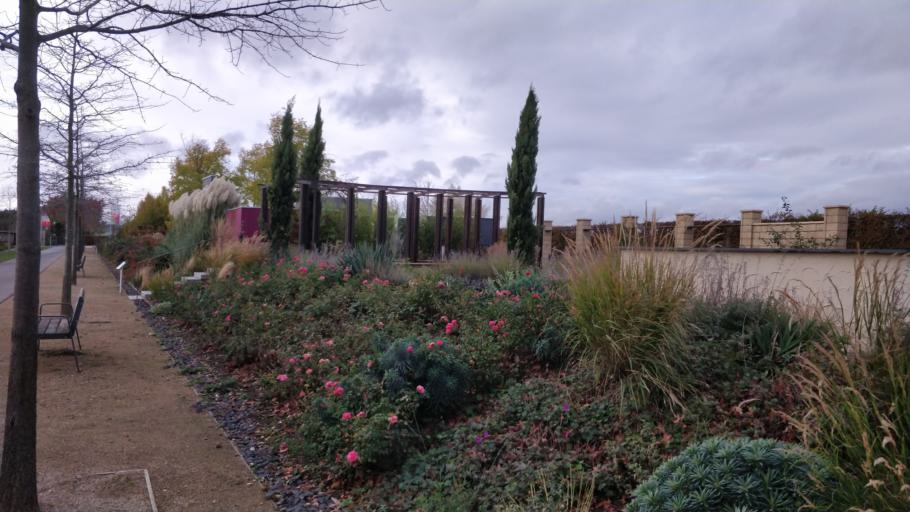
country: DE
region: North Rhine-Westphalia
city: Zulpich
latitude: 50.6819
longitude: 6.6550
